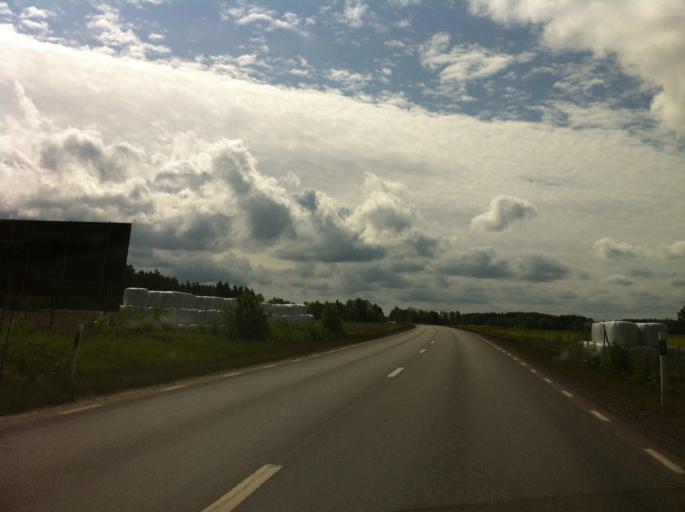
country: SE
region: Vaermland
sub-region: Karlstads Kommun
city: Edsvalla
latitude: 59.5090
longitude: 13.2135
